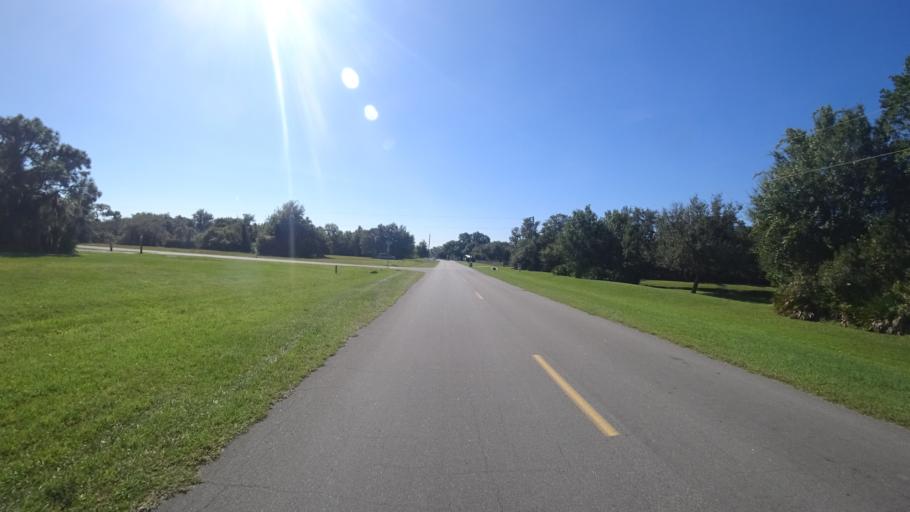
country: US
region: Florida
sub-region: Sarasota County
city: Lake Sarasota
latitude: 27.3521
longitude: -82.2509
